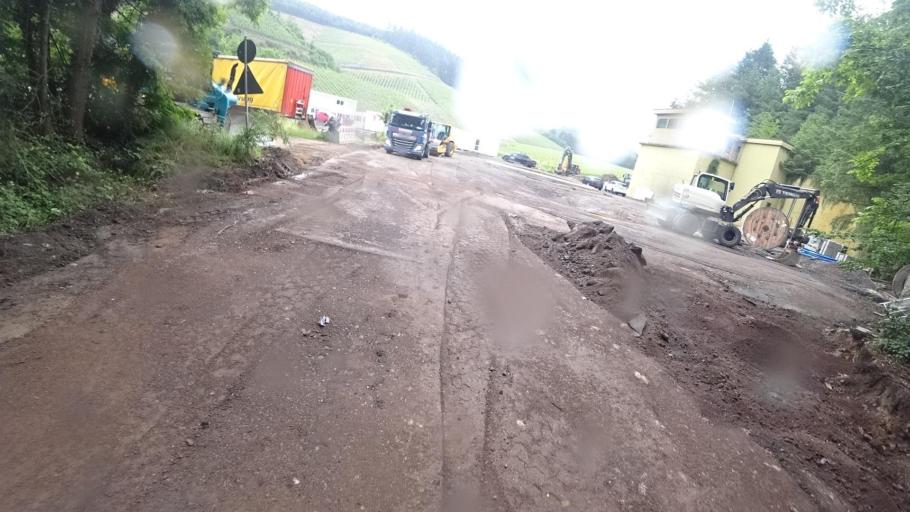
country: DE
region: Rheinland-Pfalz
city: Dernau
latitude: 50.5396
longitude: 7.0612
